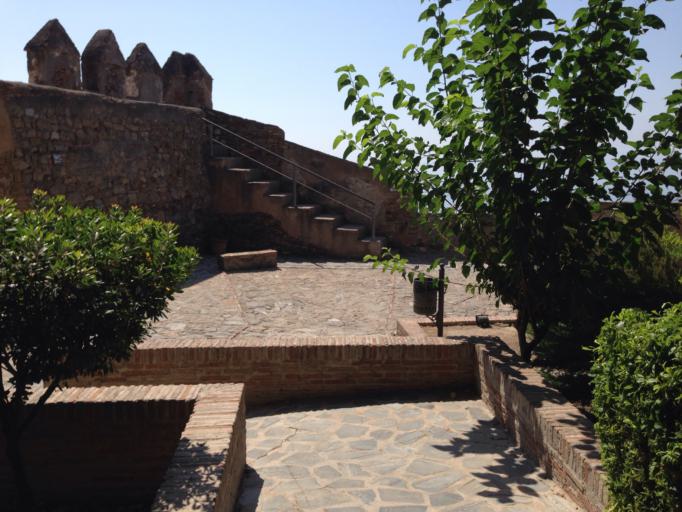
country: ES
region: Andalusia
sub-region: Provincia de Malaga
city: Malaga
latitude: 36.7234
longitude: -4.4113
